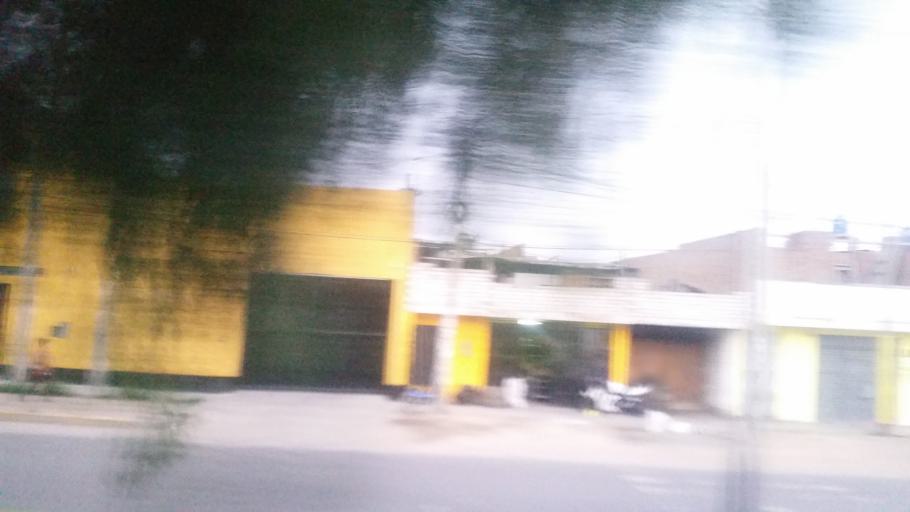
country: PE
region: La Libertad
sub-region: Provincia de Trujillo
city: La Esperanza
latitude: -8.0880
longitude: -79.0396
